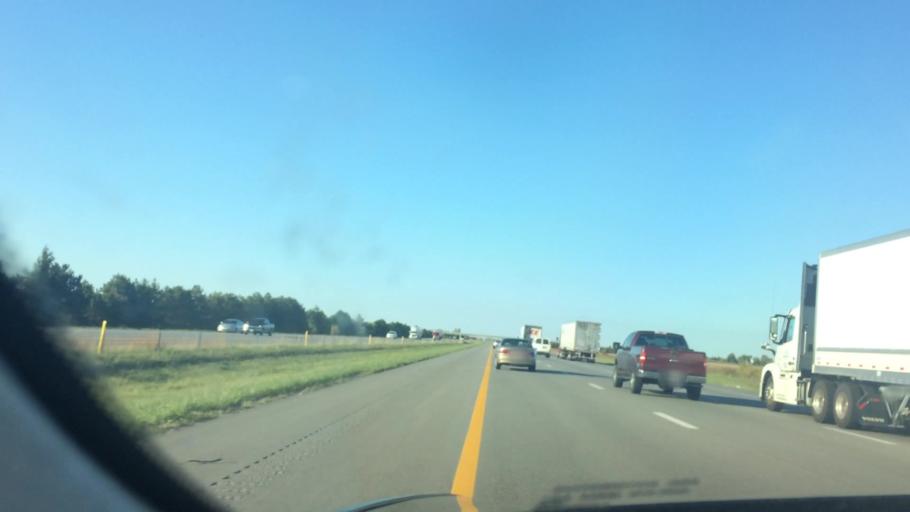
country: US
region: Ohio
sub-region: Wood County
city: Bowling Green
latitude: 41.4026
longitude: -83.6157
